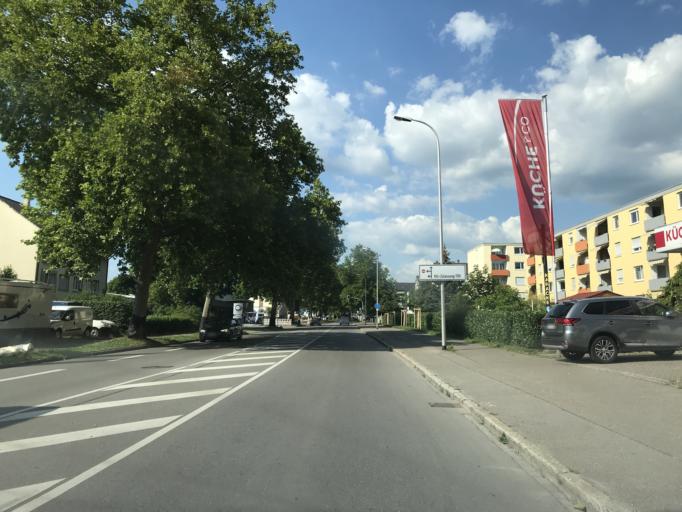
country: DE
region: Baden-Wuerttemberg
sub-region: Freiburg Region
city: Loerrach
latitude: 47.6236
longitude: 7.6761
